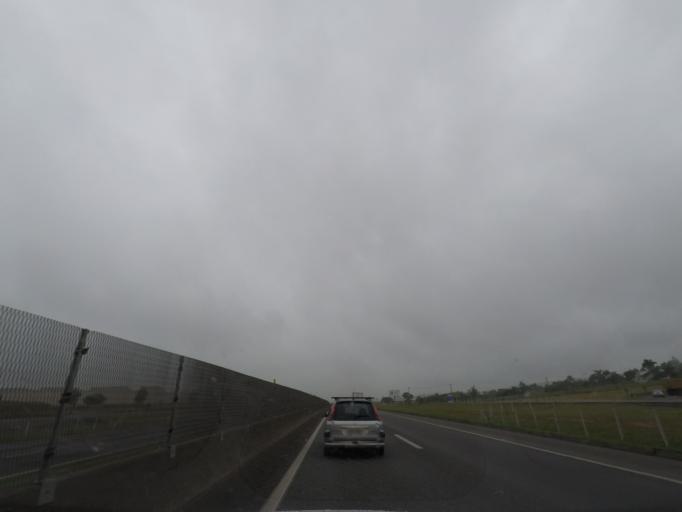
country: BR
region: Sao Paulo
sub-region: Taubate
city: Taubate
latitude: -23.0593
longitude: -45.6202
